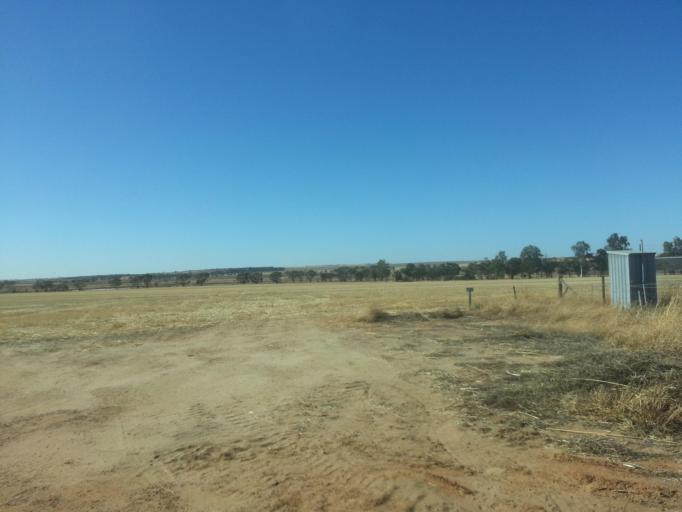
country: AU
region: Western Australia
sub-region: Wongan-Ballidu
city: Wongan Hills
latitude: -30.5833
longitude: 116.9834
